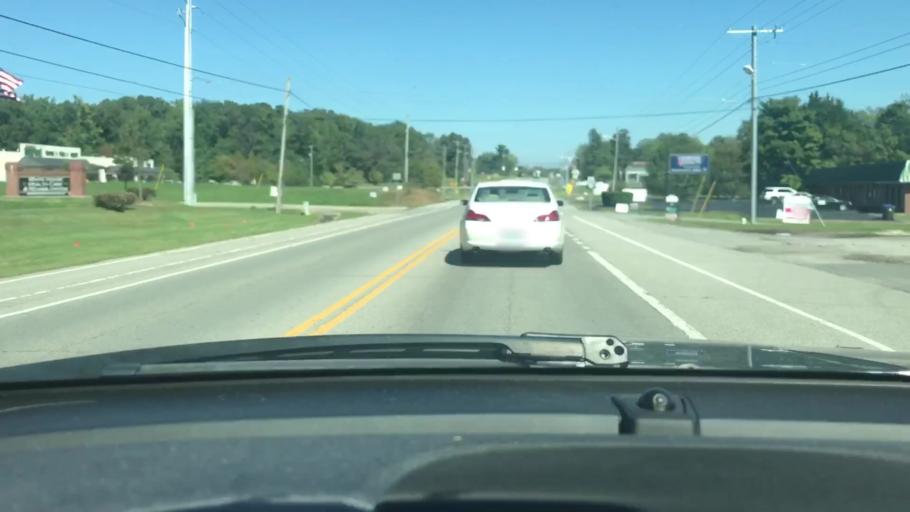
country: US
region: Tennessee
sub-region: Sumner County
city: White House
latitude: 36.4597
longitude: -86.6648
